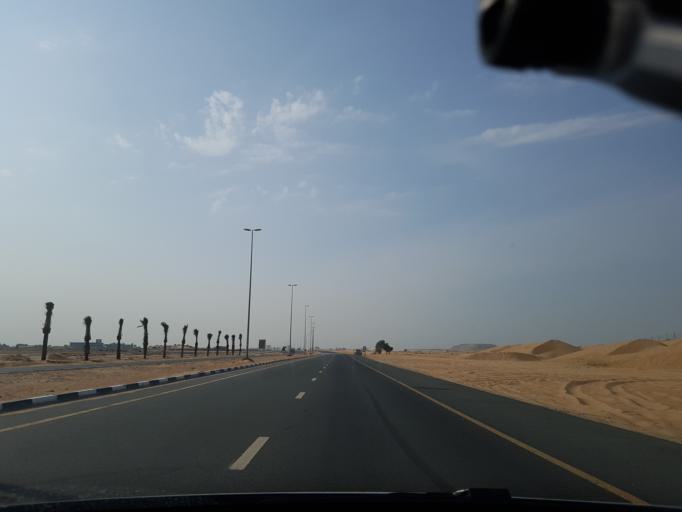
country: AE
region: Ajman
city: Ajman
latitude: 25.4075
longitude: 55.5743
